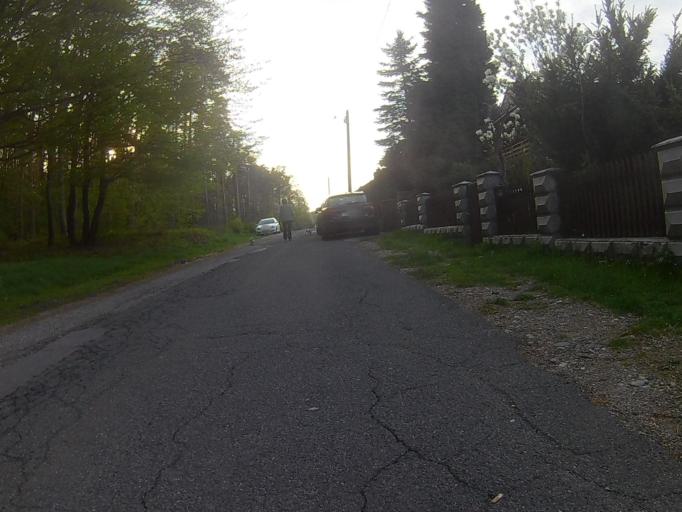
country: SI
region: Maribor
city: Pekre
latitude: 46.5361
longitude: 15.5935
